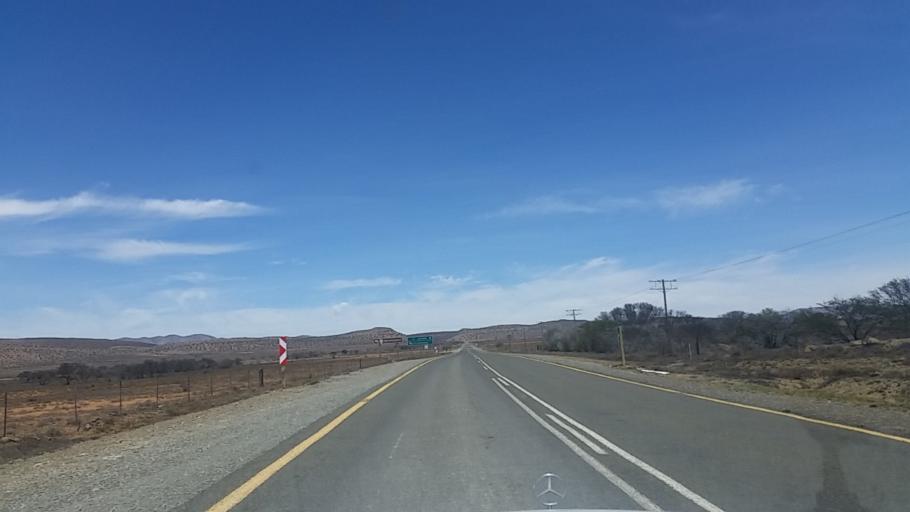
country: ZA
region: Eastern Cape
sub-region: Cacadu District Municipality
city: Willowmore
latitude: -33.3173
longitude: 23.4635
